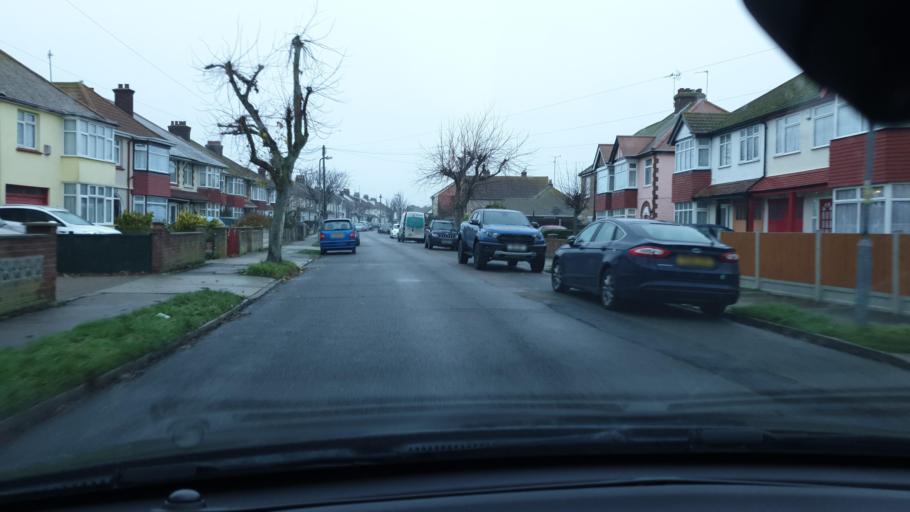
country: GB
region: England
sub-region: Essex
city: Clacton-on-Sea
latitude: 51.7894
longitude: 1.1443
